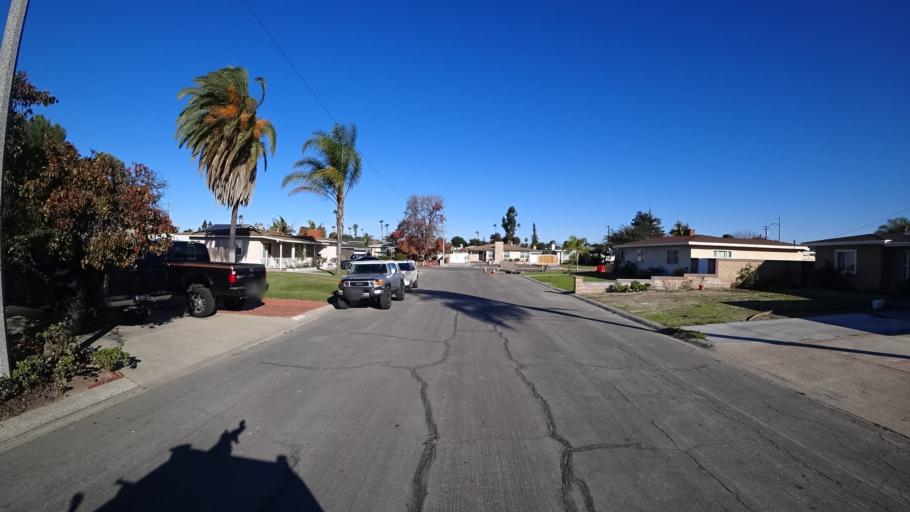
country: US
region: California
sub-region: Orange County
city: Garden Grove
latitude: 33.7694
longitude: -117.9698
